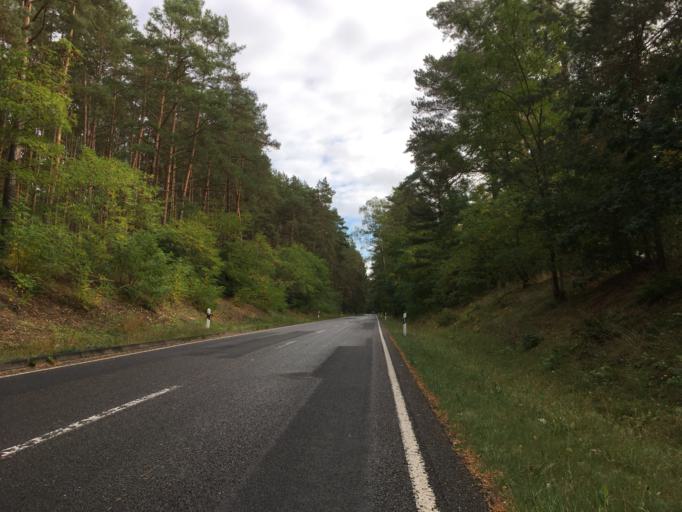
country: DE
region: Brandenburg
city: Oderberg
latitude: 52.8870
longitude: 14.0838
